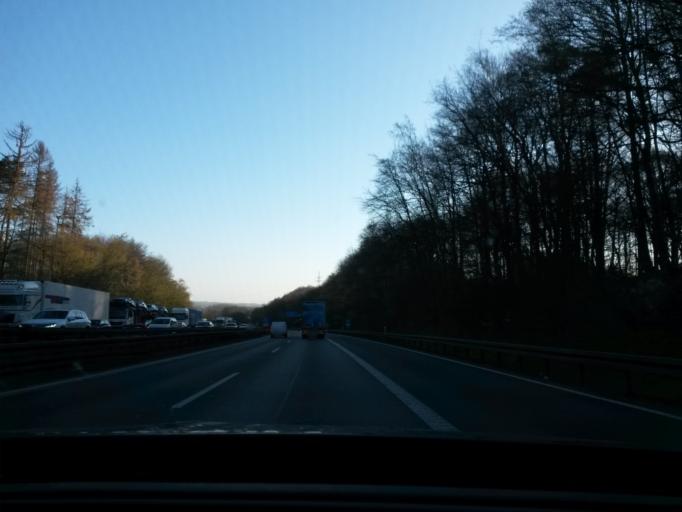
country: DE
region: North Rhine-Westphalia
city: Schwerte
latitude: 51.4054
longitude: 7.5453
